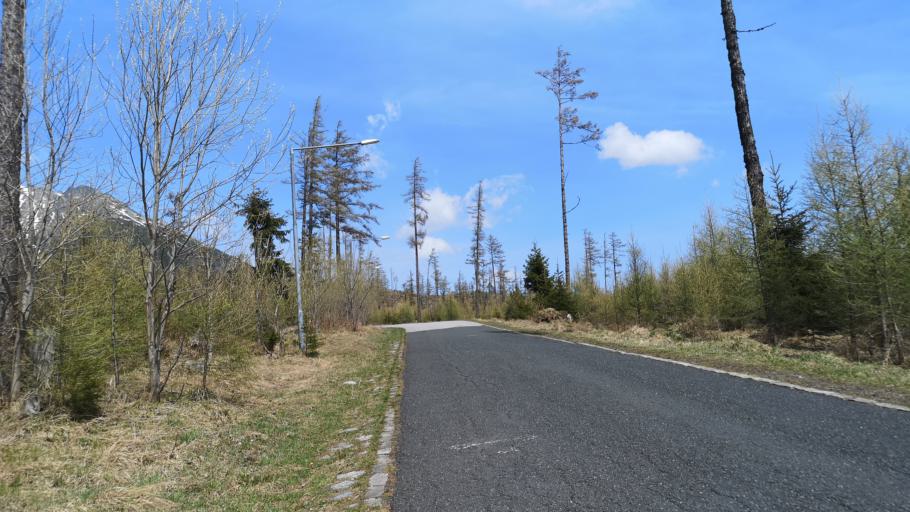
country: SK
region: Presovsky
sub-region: Okres Poprad
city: Vysoke Tatry
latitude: 49.1523
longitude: 20.2258
